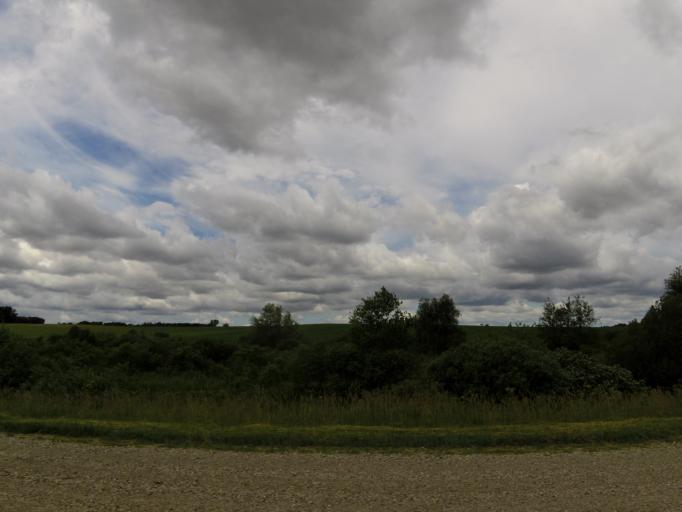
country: US
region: Iowa
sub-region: Howard County
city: Cresco
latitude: 43.4492
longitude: -92.2986
